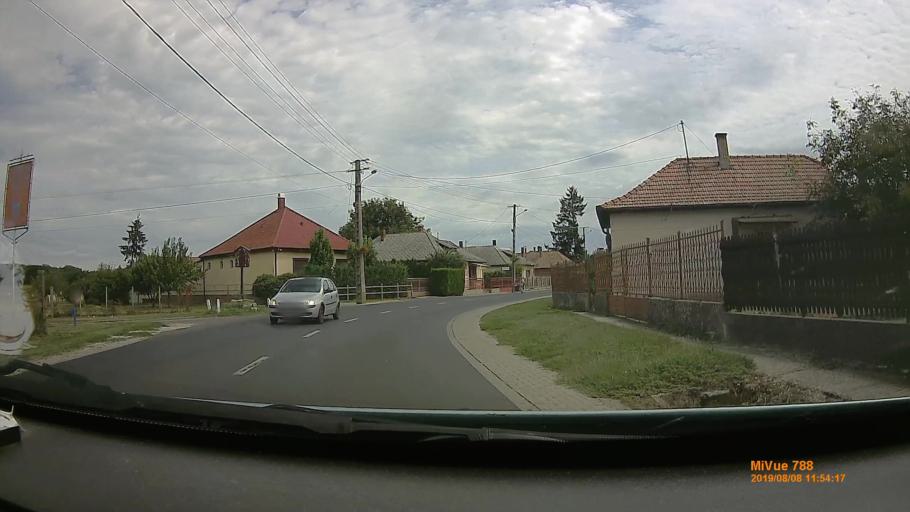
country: HU
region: Szabolcs-Szatmar-Bereg
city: Nyirmihalydi
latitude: 47.7344
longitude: 21.9688
